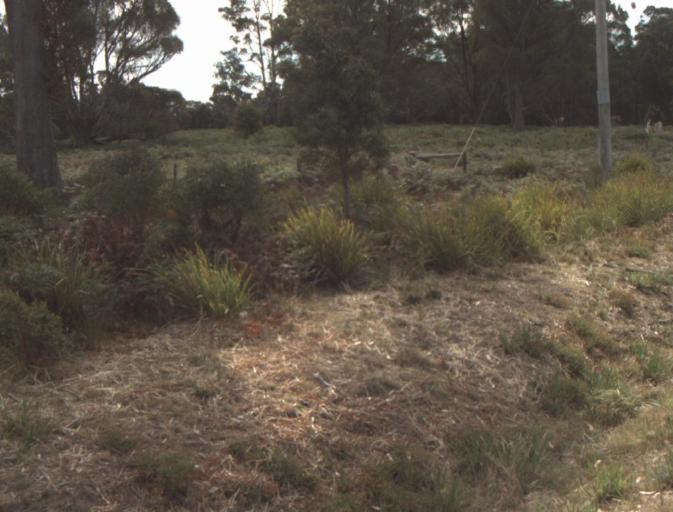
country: AU
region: Tasmania
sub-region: Launceston
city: Mayfield
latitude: -41.2774
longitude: 147.0373
